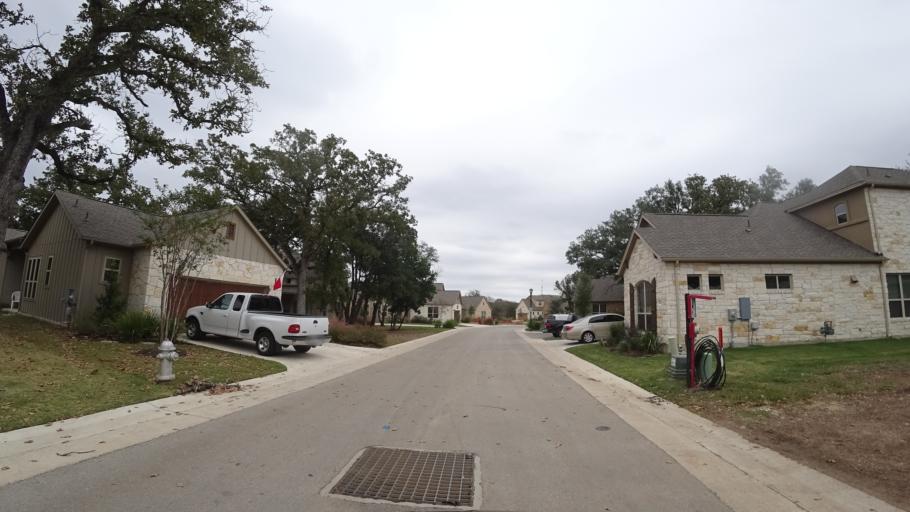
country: US
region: Texas
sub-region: Travis County
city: Shady Hollow
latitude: 30.1485
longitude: -97.8521
